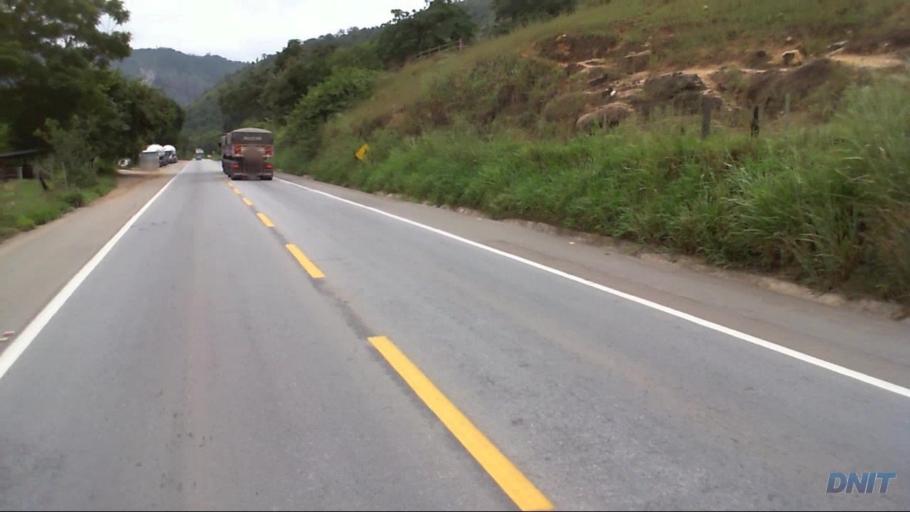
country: BR
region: Minas Gerais
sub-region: Timoteo
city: Timoteo
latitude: -19.5648
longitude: -42.7112
